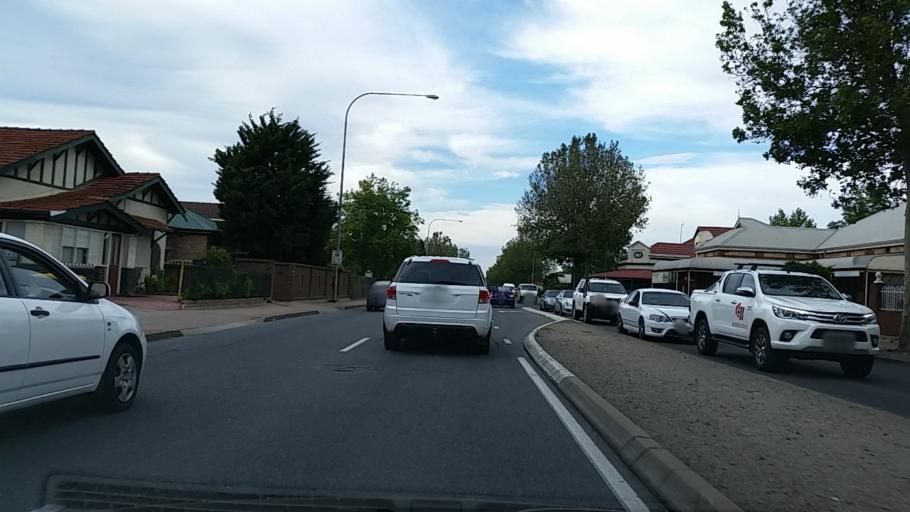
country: AU
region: South Australia
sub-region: City of West Torrens
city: Thebarton
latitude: -34.9302
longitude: 138.5702
